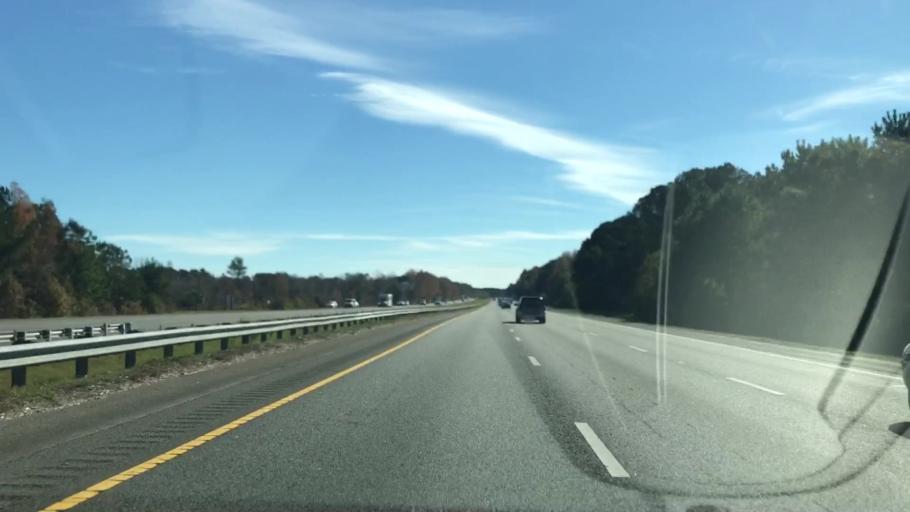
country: US
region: South Carolina
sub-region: Berkeley County
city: Ladson
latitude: 32.9978
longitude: -80.0934
